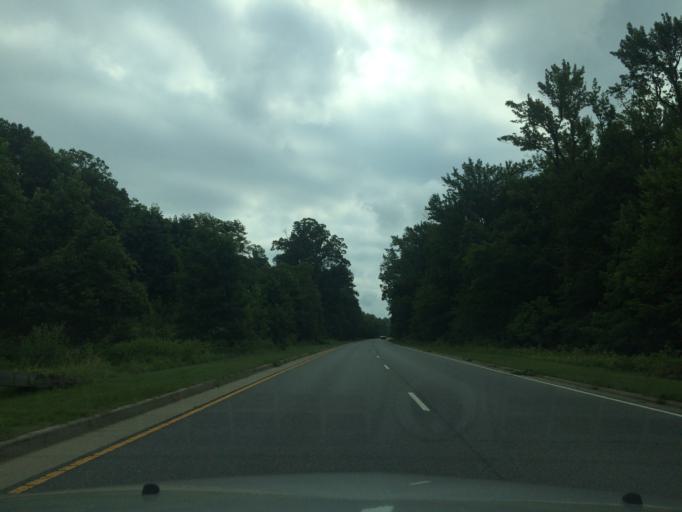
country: US
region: Maryland
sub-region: Prince George's County
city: Morningside
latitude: 38.8353
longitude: -76.8902
